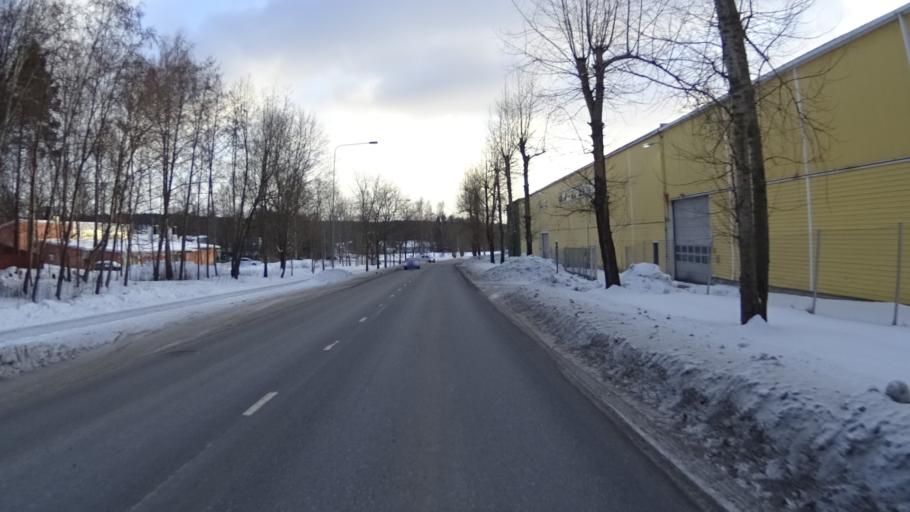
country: FI
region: Uusimaa
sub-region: Helsinki
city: Lohja
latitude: 60.2540
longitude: 24.0579
